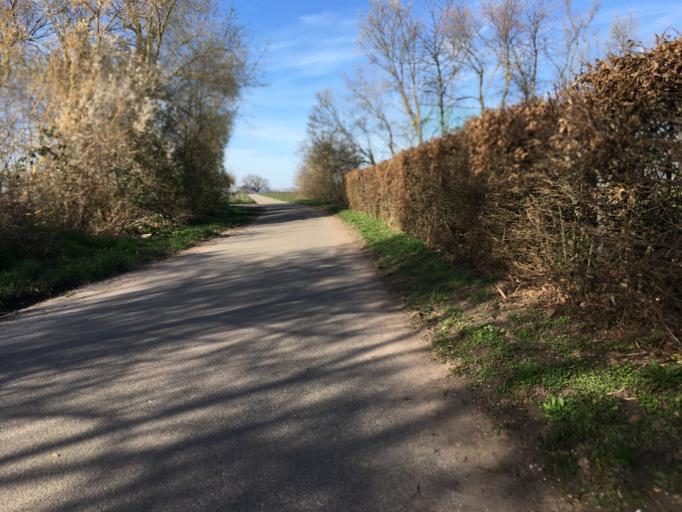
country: DE
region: Rheinland-Pfalz
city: Kirrweiler
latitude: 49.3203
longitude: 8.1587
